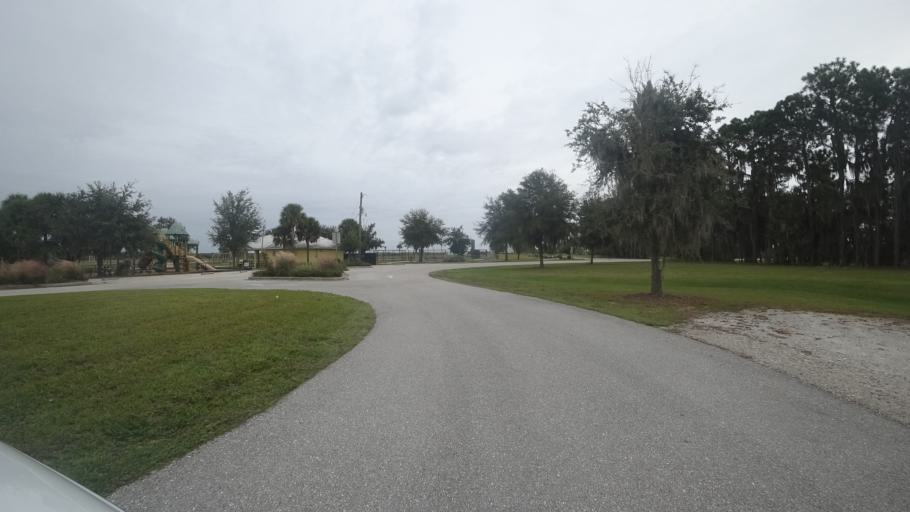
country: US
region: Florida
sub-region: Hillsborough County
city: Wimauma
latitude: 27.5844
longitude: -82.1771
